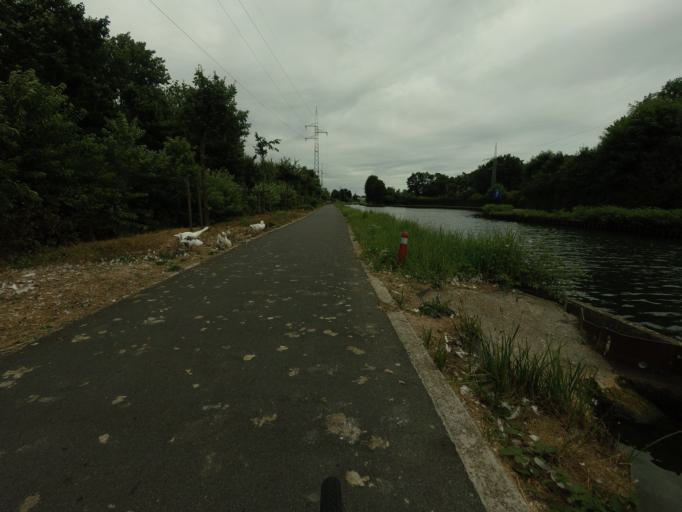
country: BE
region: Flanders
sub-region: Provincie Antwerpen
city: Brasschaat
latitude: 51.2914
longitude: 4.5451
